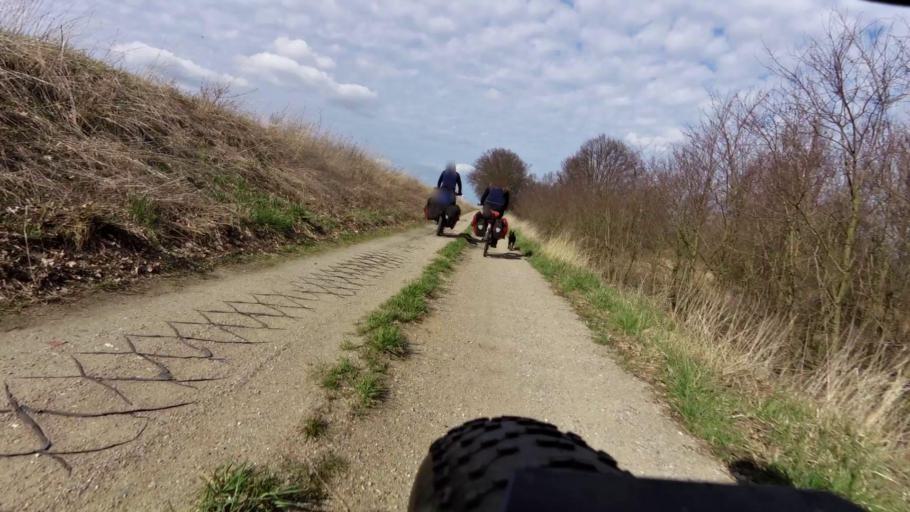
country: DE
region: Brandenburg
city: Reitwein
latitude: 52.4647
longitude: 14.6136
